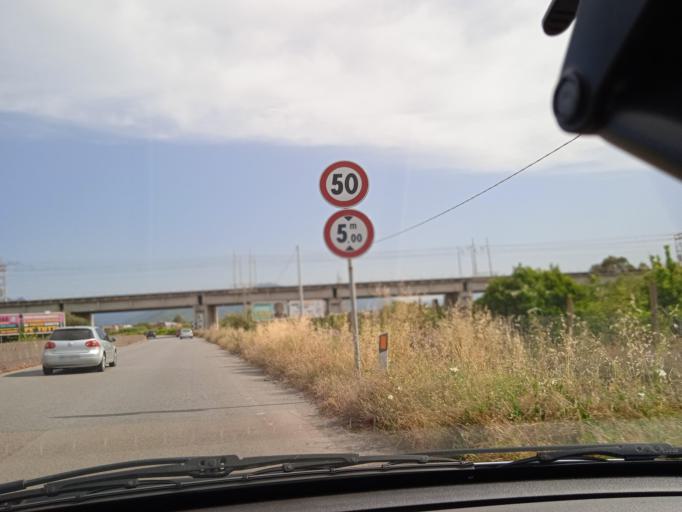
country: IT
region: Sicily
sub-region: Messina
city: Milazzo
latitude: 38.2004
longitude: 15.2468
